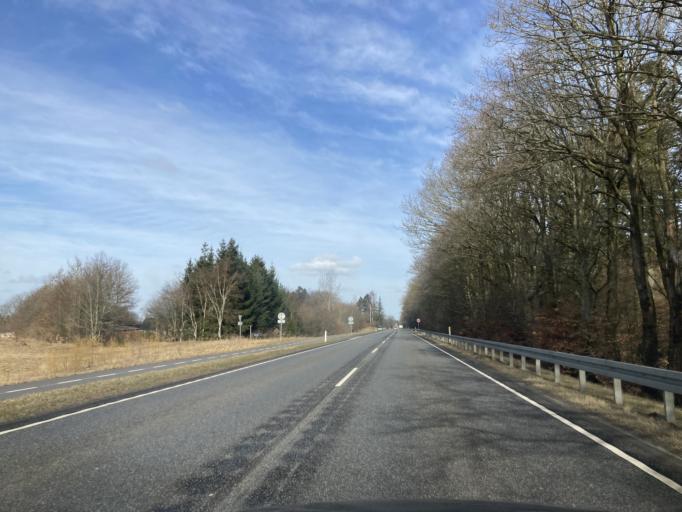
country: DK
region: Central Jutland
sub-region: Hedensted Kommune
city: Torring
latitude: 55.9978
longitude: 9.3862
